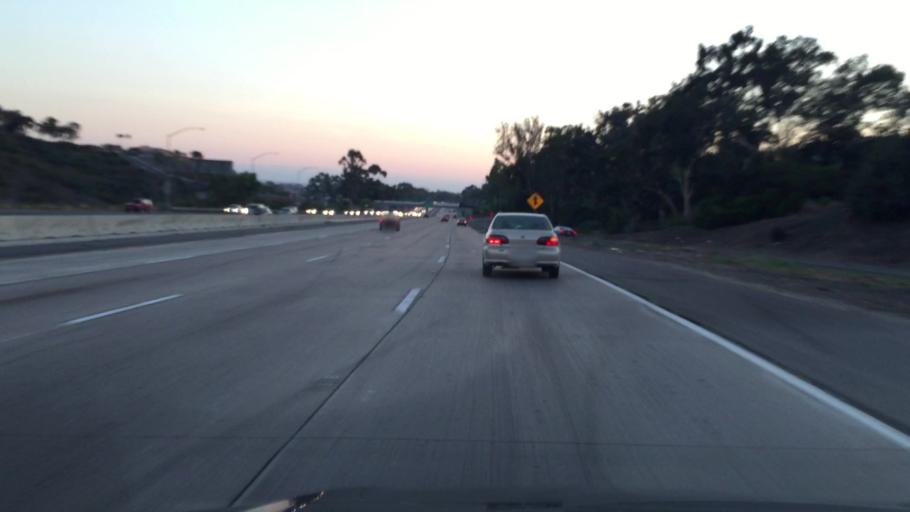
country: US
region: California
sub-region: San Diego County
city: Lemon Grove
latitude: 32.7269
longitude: -117.0722
